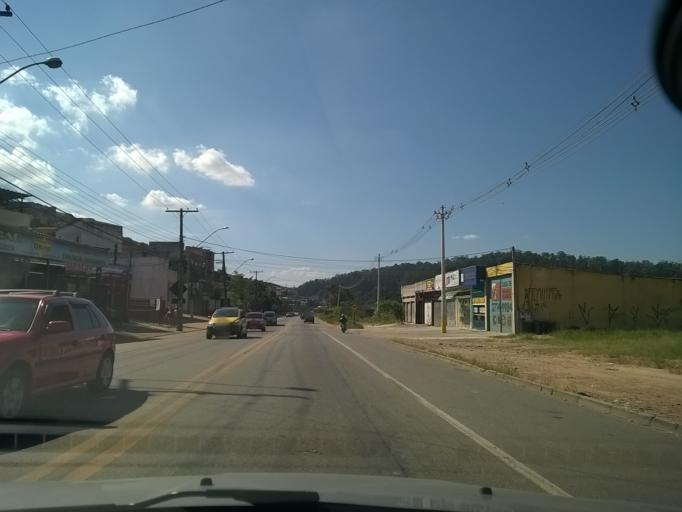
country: BR
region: Sao Paulo
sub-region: Caieiras
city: Caieiras
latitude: -23.3461
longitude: -46.7428
